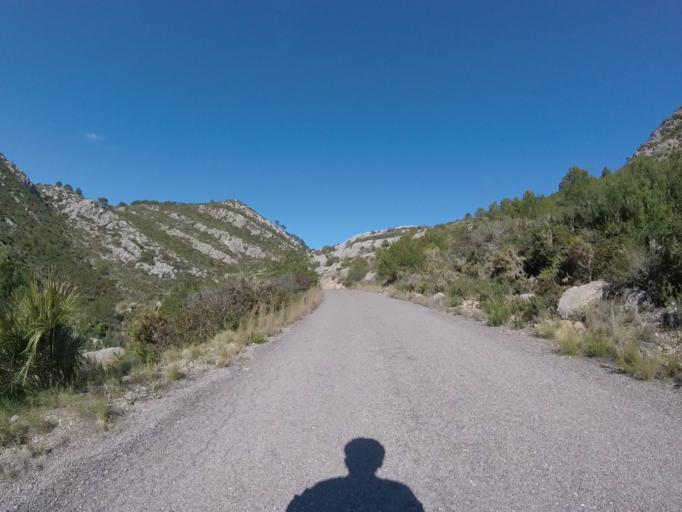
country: ES
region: Valencia
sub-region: Provincia de Castello
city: Benicassim
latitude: 40.0773
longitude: 0.1051
